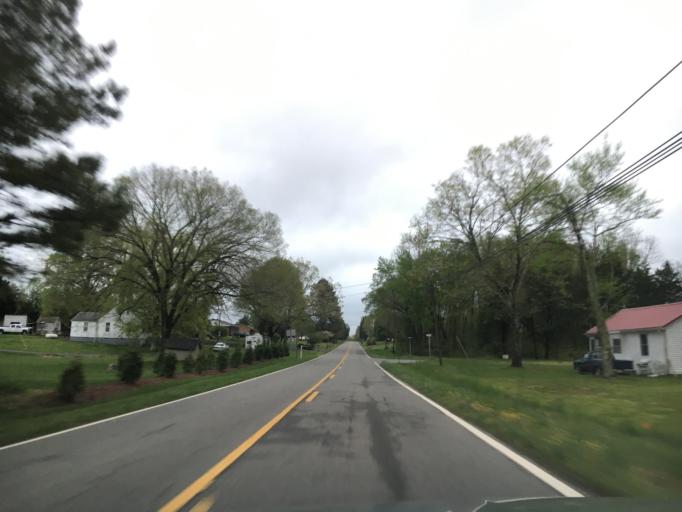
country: US
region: Virginia
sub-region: Halifax County
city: South Boston
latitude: 36.6552
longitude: -78.8765
